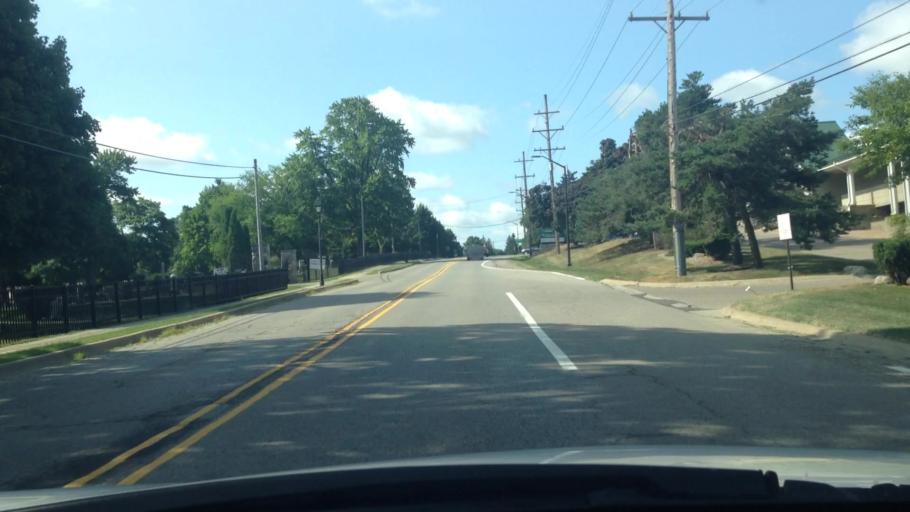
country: US
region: Michigan
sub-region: Oakland County
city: Clarkston
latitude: 42.7279
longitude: -83.4287
